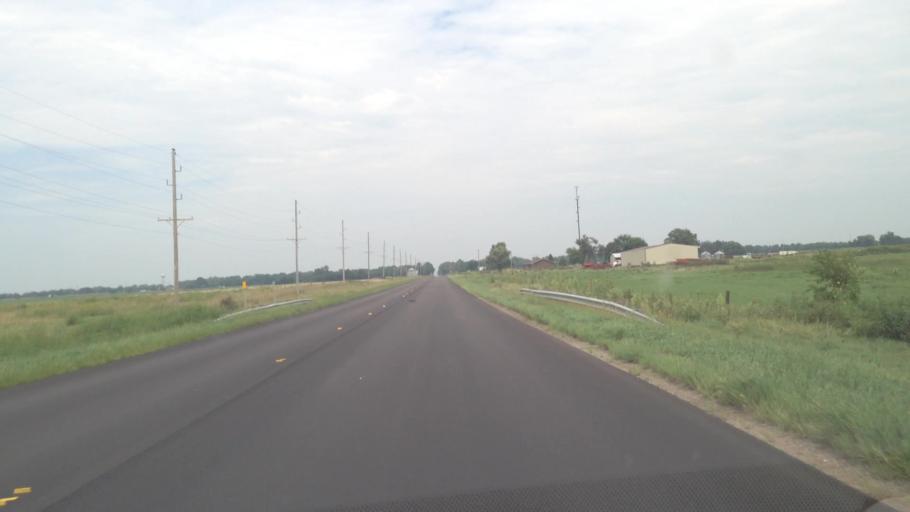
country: US
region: Kansas
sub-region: Allen County
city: Iola
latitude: 37.8976
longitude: -95.1705
